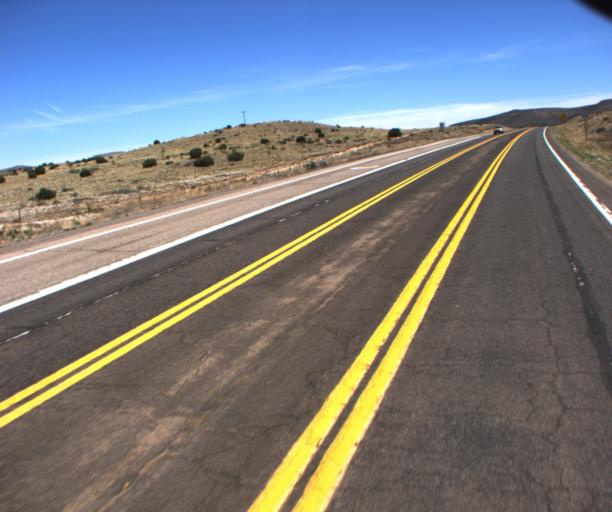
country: US
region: Arizona
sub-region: Mohave County
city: Peach Springs
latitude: 35.5239
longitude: -113.4721
